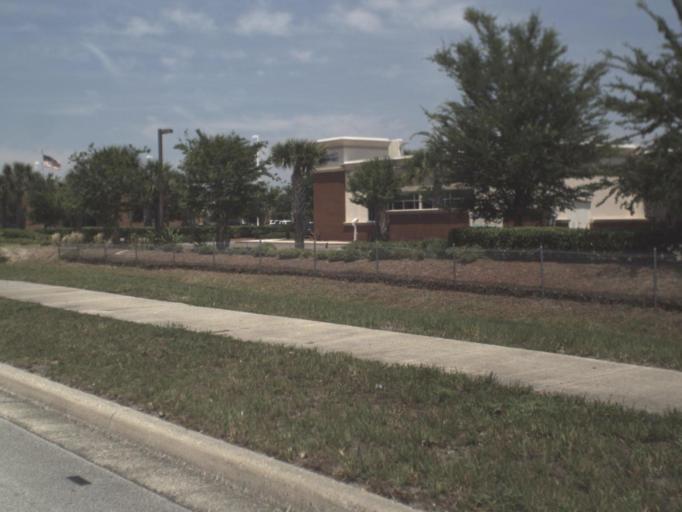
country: US
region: Florida
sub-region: Saint Johns County
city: Ponte Vedra Beach
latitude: 30.2160
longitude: -81.5159
